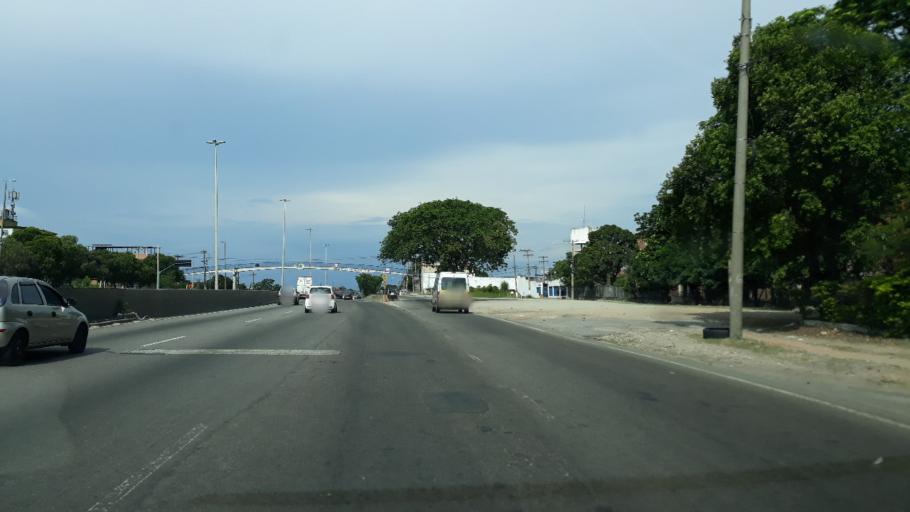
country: BR
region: Rio de Janeiro
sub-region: Sao Joao De Meriti
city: Sao Joao de Meriti
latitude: -22.8318
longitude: -43.3524
